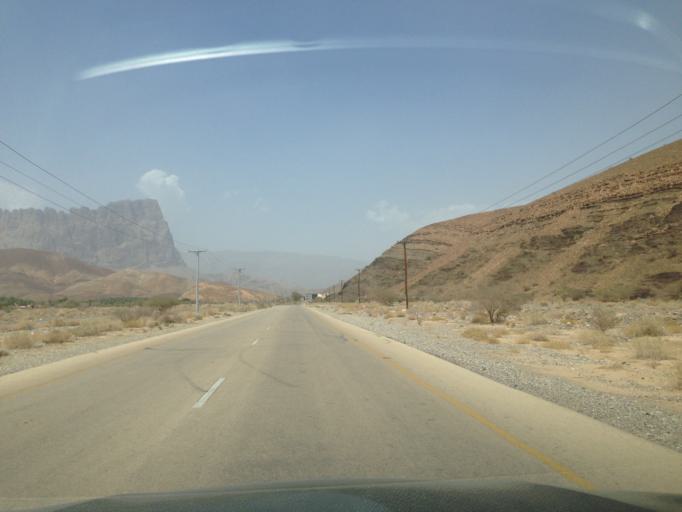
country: OM
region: Az Zahirah
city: `Ibri
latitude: 23.1998
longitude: 56.9396
